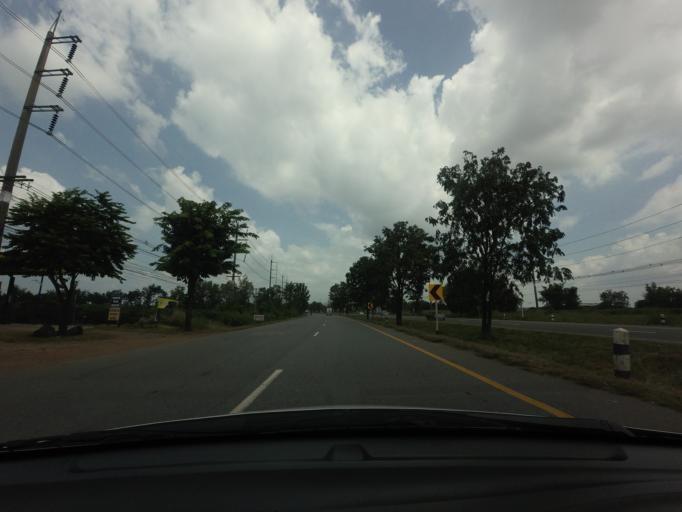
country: TH
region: Prachin Buri
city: Kabin Buri
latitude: 13.9057
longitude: 101.6609
